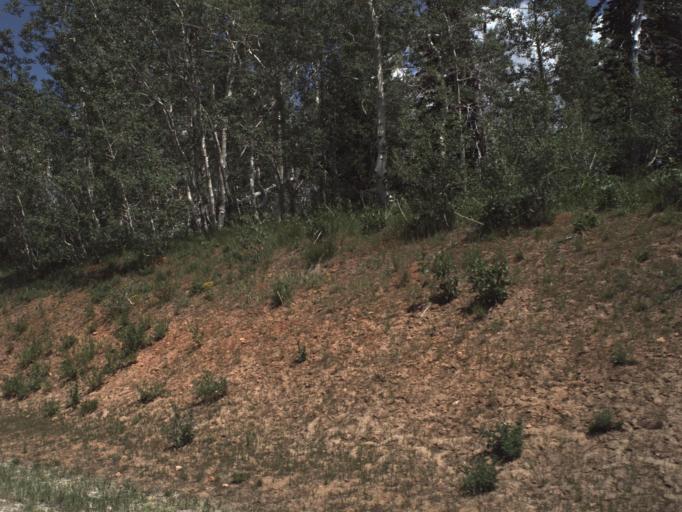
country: US
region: Utah
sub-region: Weber County
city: Wolf Creek
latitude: 41.4686
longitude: -111.4918
